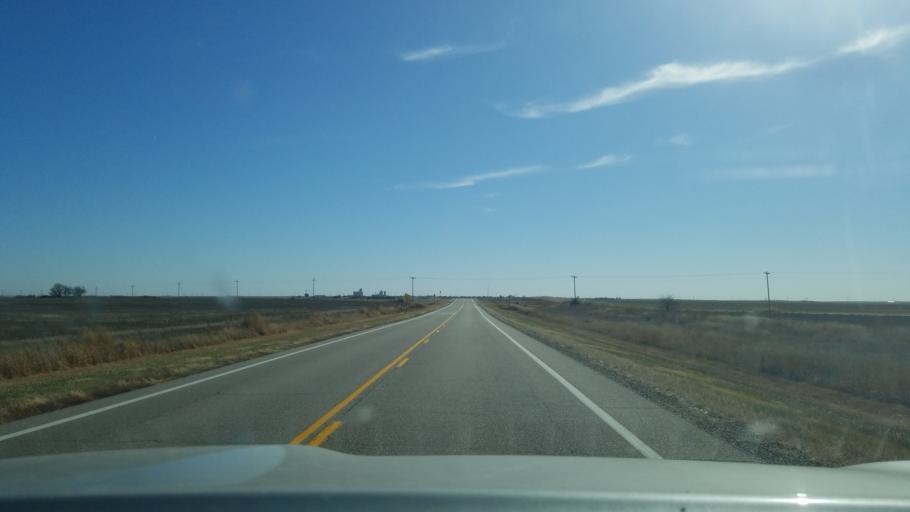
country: US
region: Kansas
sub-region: Kiowa County
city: Greensburg
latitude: 37.5731
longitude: -99.6664
